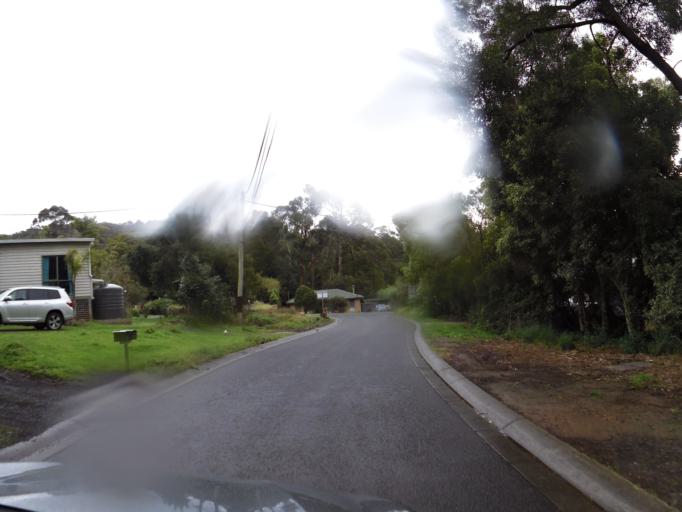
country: AU
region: Victoria
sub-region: Knox
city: The Basin
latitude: -37.8620
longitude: 145.3251
